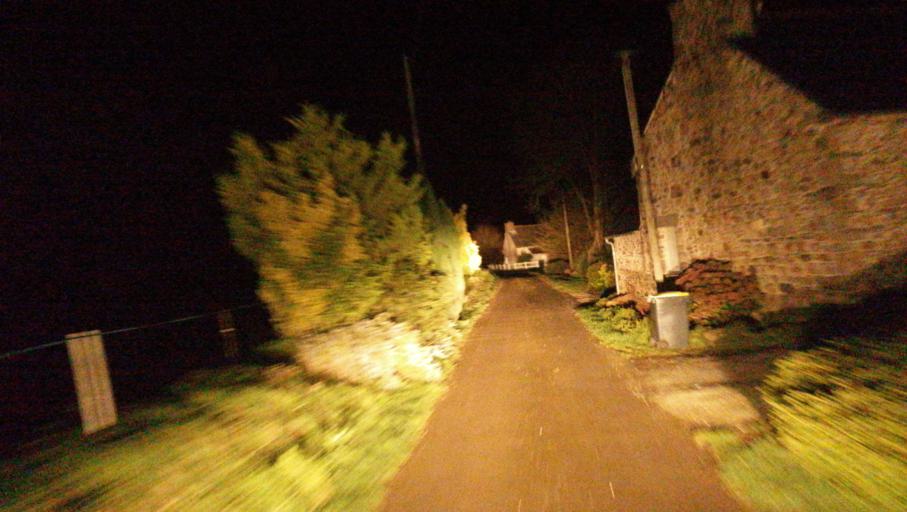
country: FR
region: Brittany
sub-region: Departement des Cotes-d'Armor
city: Lanvollon
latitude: 48.6386
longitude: -3.0095
